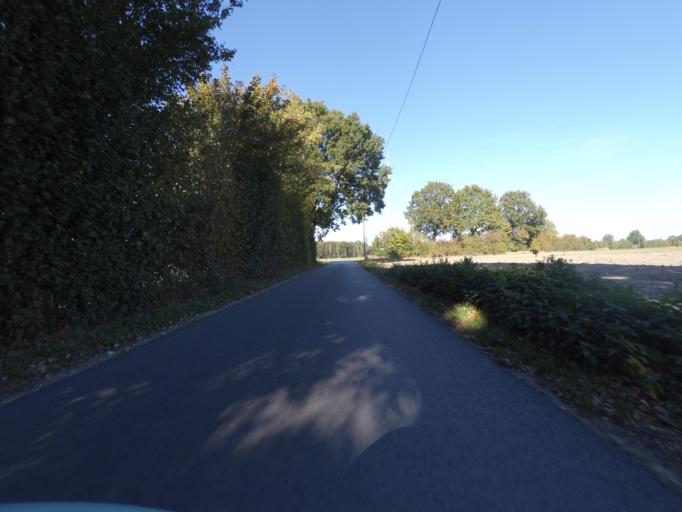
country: NL
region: Gelderland
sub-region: Gemeente Aalten
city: Aalten
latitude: 51.8721
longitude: 6.5718
